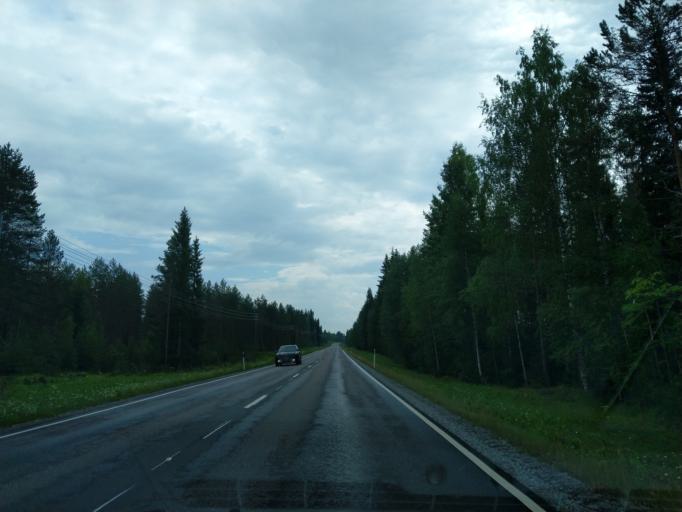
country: FI
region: Southern Savonia
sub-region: Savonlinna
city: Punkaharju
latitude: 61.6467
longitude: 29.4240
